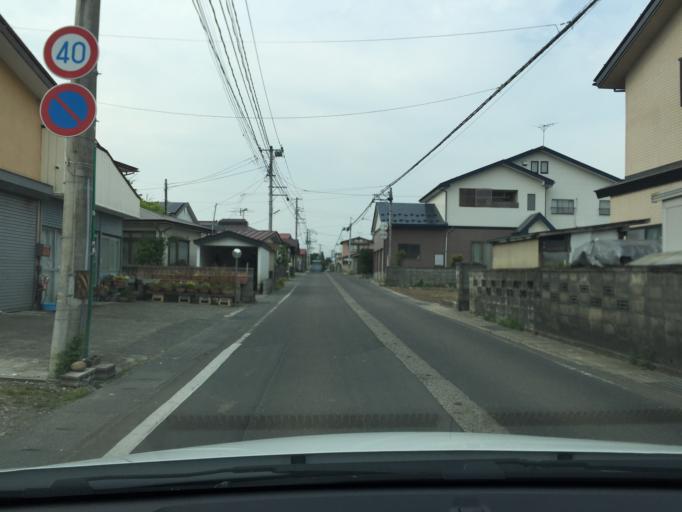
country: JP
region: Fukushima
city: Kitakata
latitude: 37.5435
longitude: 139.9286
